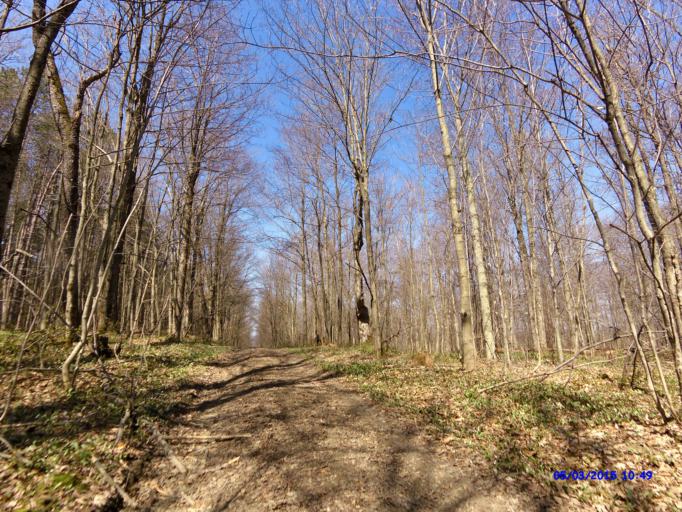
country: US
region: New York
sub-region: Cattaraugus County
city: Franklinville
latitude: 42.3378
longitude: -78.4125
